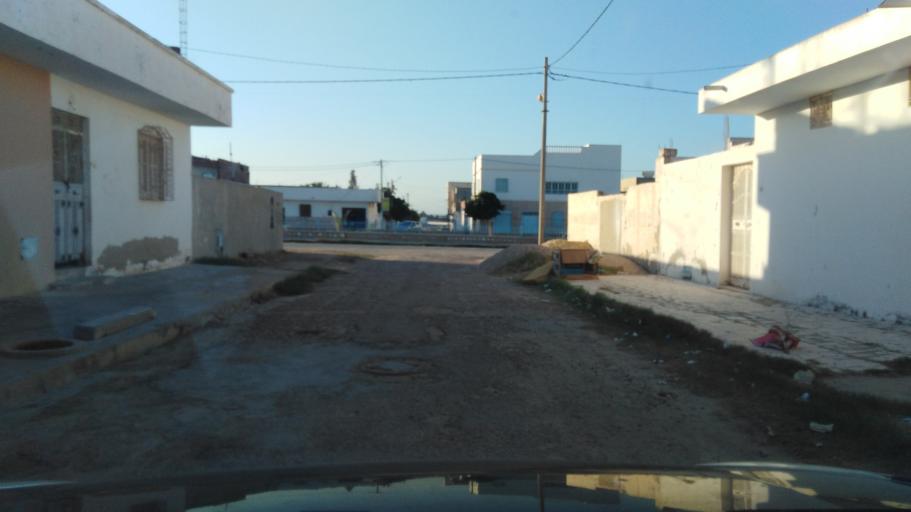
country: TN
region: Qabis
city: Gabes
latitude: 33.9528
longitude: 10.0126
